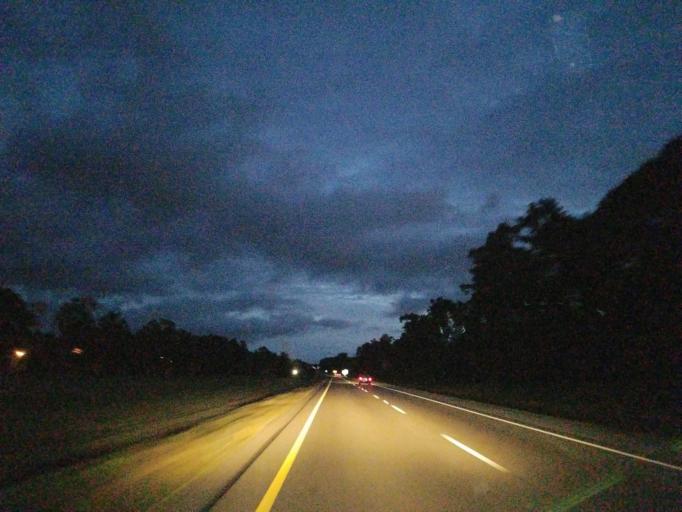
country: US
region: Mississippi
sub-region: Jones County
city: Sharon
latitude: 31.8069
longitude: -89.0537
